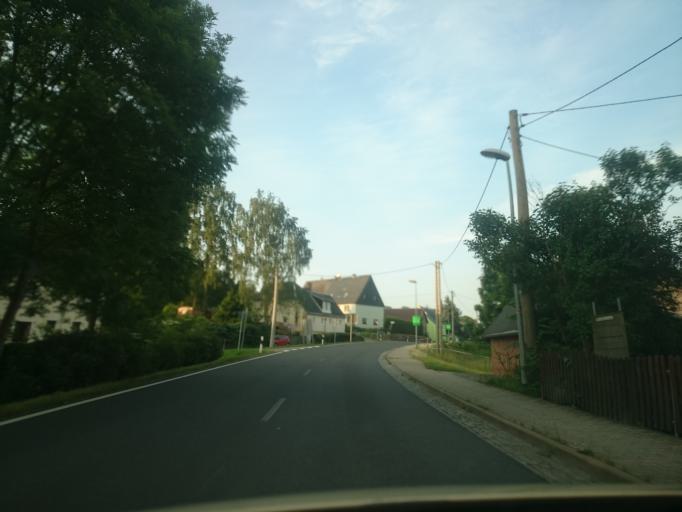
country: DE
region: Saxony
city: Grosshartmannsdorf
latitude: 50.7940
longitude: 13.3187
